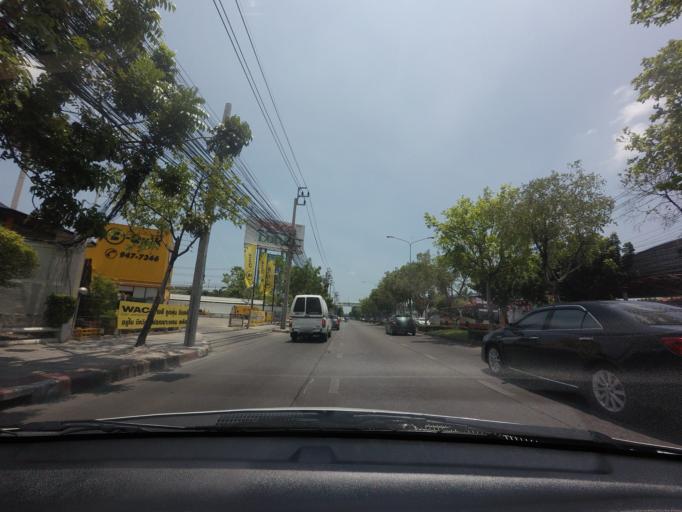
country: TH
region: Bangkok
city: Khan Na Yao
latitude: 13.8249
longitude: 100.6567
